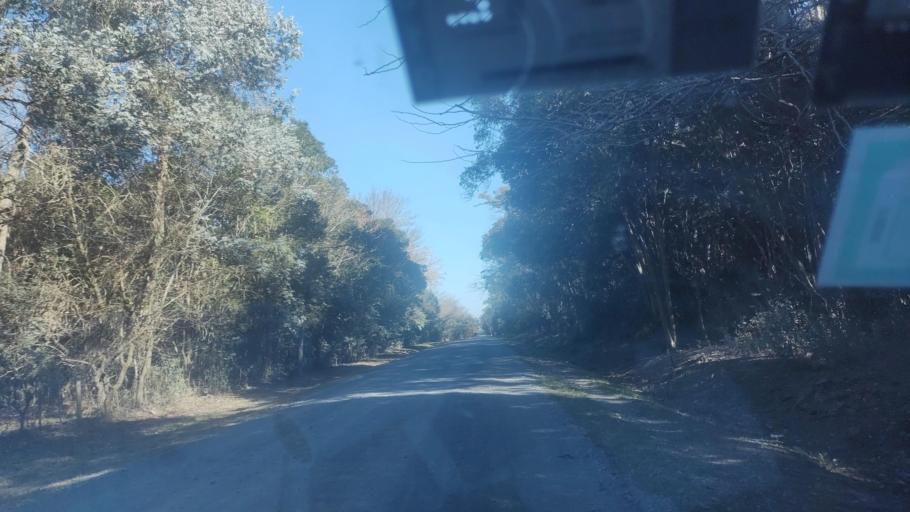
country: AR
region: Buenos Aires
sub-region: Partido de La Plata
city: La Plata
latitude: -34.8517
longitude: -58.1041
